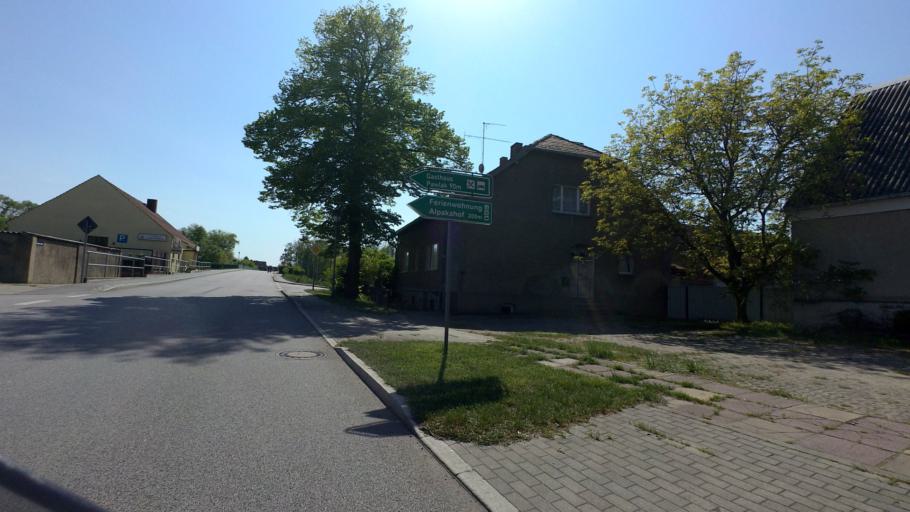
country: DE
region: Brandenburg
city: Tauche
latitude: 52.0866
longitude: 14.1713
